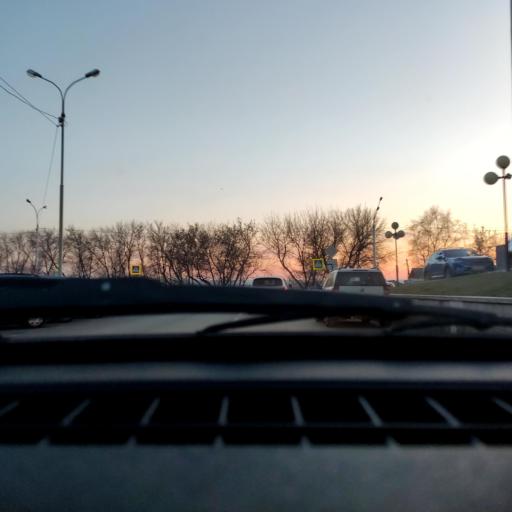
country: RU
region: Bashkortostan
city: Ufa
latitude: 54.7183
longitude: 55.9373
